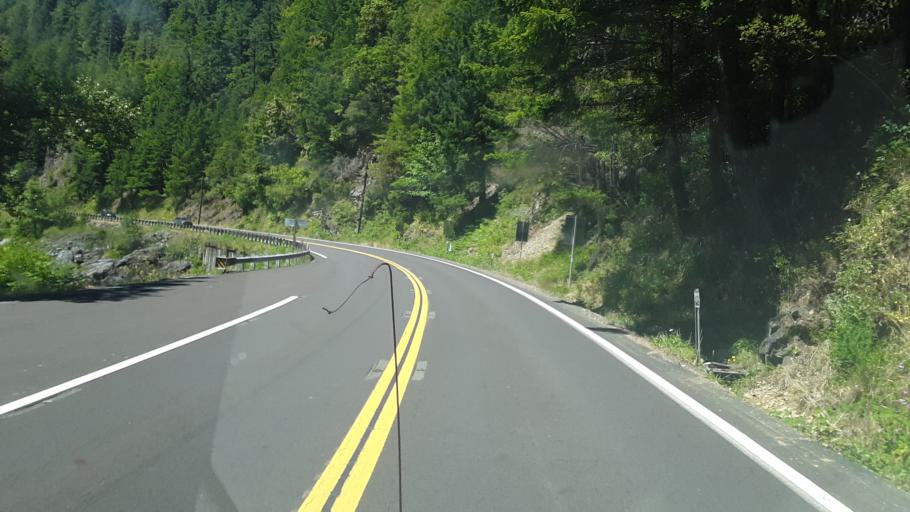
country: US
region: California
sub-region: Del Norte County
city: Bertsch-Oceanview
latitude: 41.8395
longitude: -124.0350
